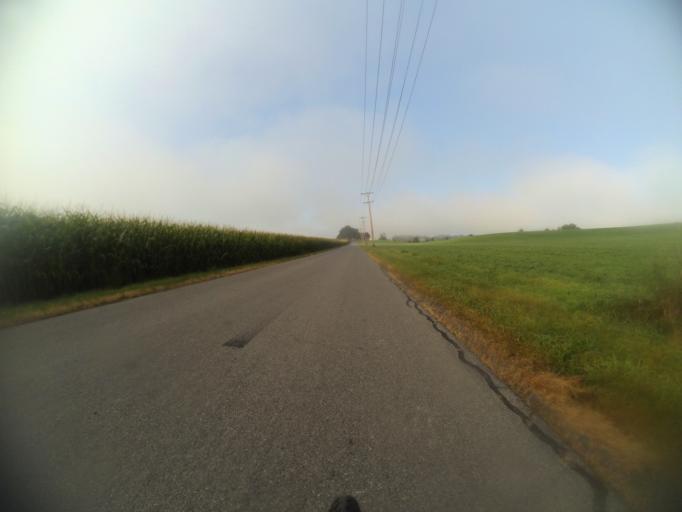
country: US
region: Pennsylvania
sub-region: Centre County
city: Centre Hall
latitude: 40.8495
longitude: -77.6632
